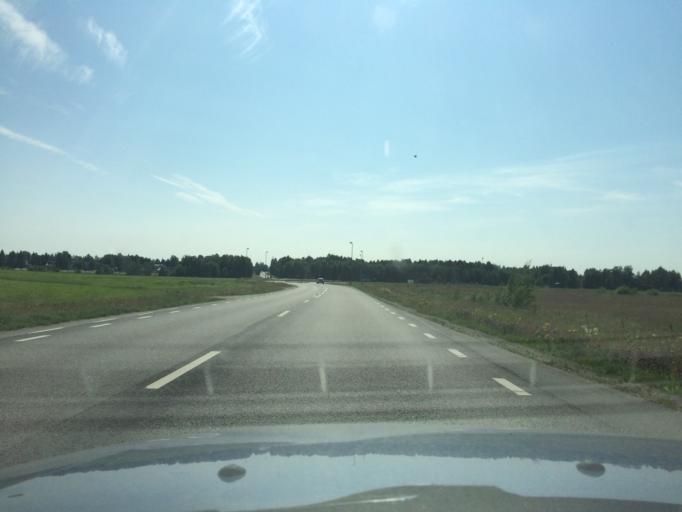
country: SE
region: Norrbotten
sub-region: Pitea Kommun
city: Bergsviken
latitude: 65.3542
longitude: 21.4015
